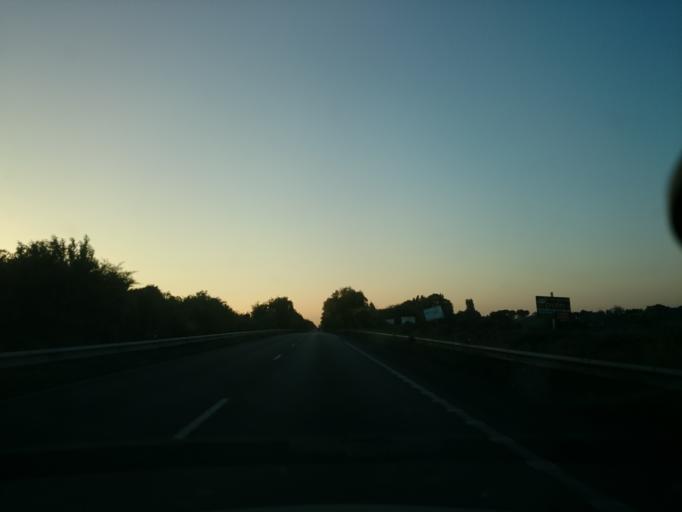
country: FR
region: Pays de la Loire
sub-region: Departement de la Loire-Atlantique
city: Jans
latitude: 47.6154
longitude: -1.6351
